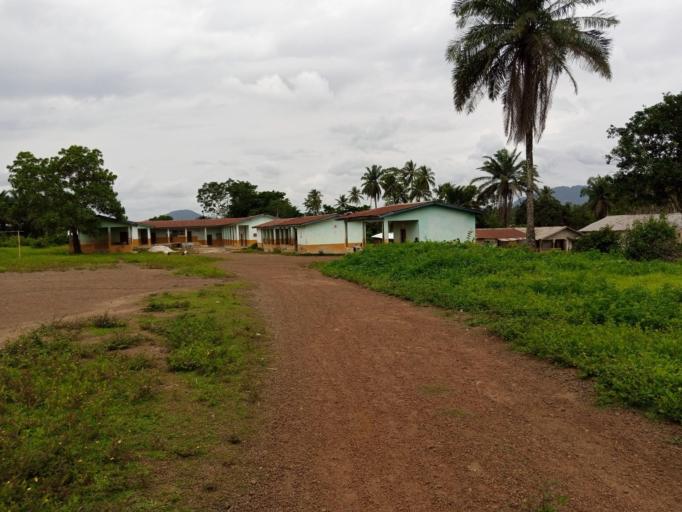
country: SL
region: Southern Province
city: Moyamba
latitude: 8.1607
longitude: -12.4250
